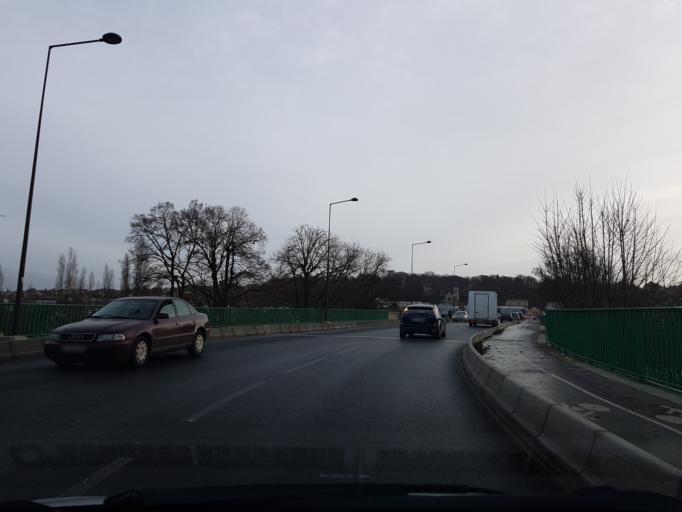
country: FR
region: Ile-de-France
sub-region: Departement du Val-de-Marne
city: Villeneuve-Saint-Georges
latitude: 48.7285
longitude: 2.4420
